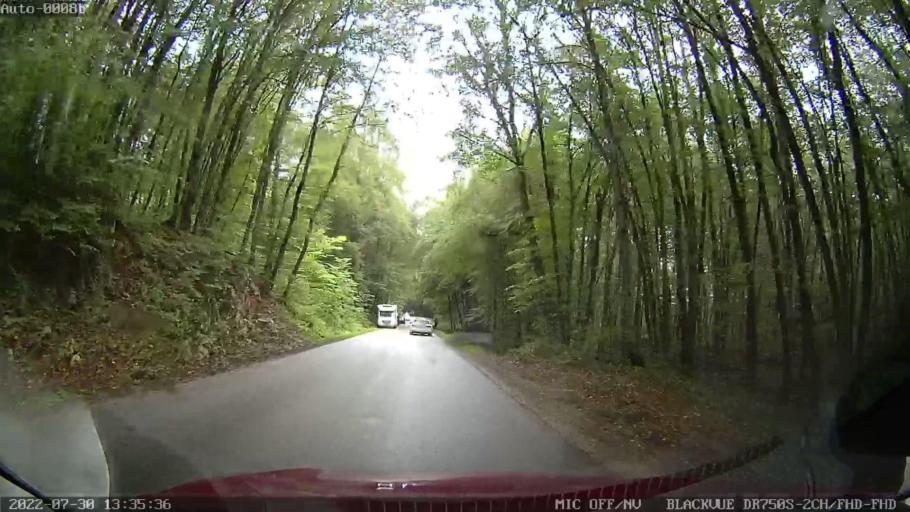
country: SI
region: Zuzemberk
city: Zuzemberk
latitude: 45.8659
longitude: 14.9265
